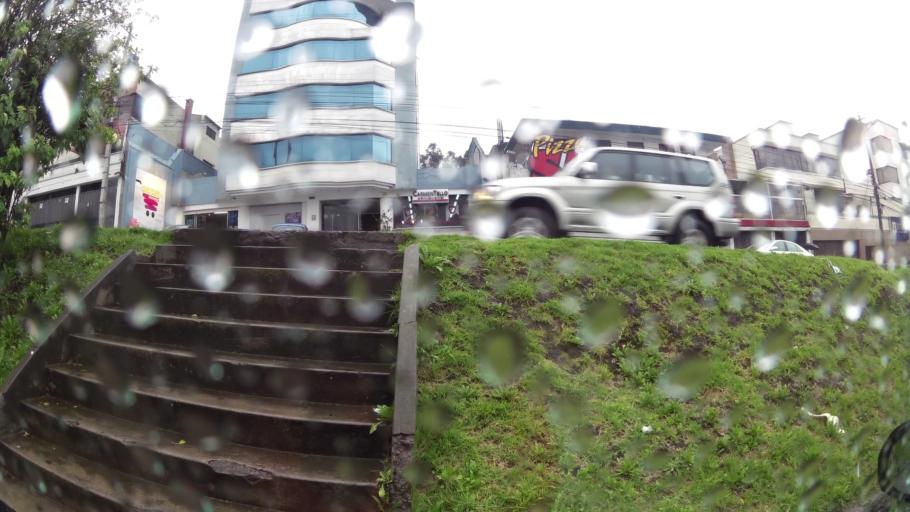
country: EC
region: Pichincha
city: Quito
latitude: -0.1621
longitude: -78.4634
